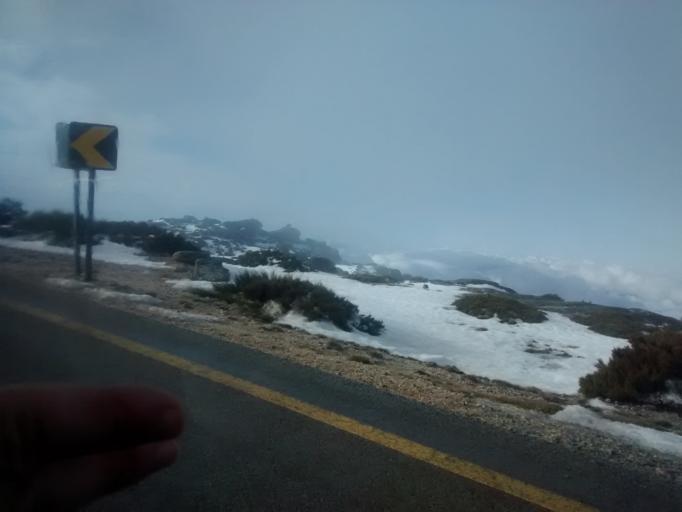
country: PT
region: Guarda
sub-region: Seia
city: Seia
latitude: 40.3473
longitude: -7.6631
